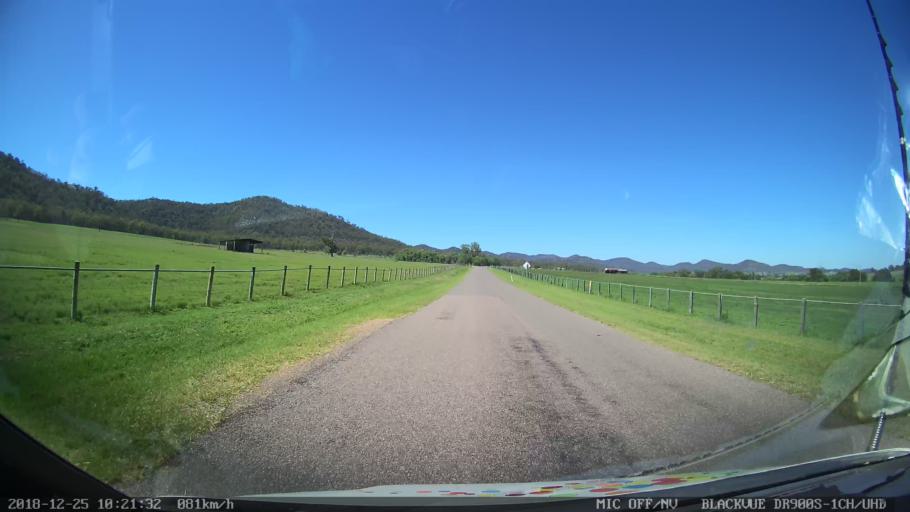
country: AU
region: New South Wales
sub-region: Muswellbrook
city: Denman
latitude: -32.3685
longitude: 150.5411
